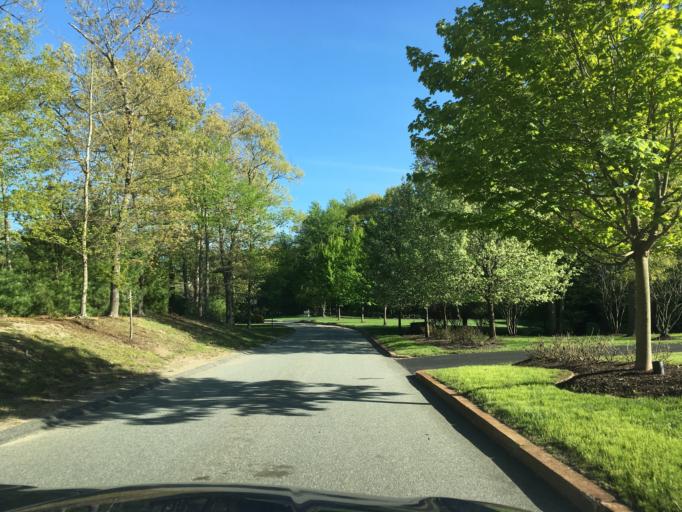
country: US
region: Rhode Island
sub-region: Washington County
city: Exeter
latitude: 41.6111
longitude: -71.5262
